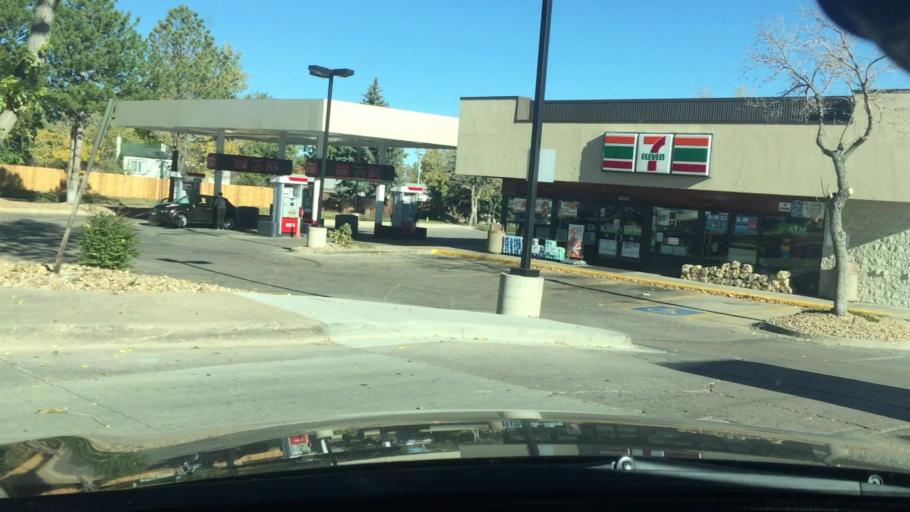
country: US
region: Colorado
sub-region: Arapahoe County
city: Dove Valley
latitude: 39.6276
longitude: -104.7956
